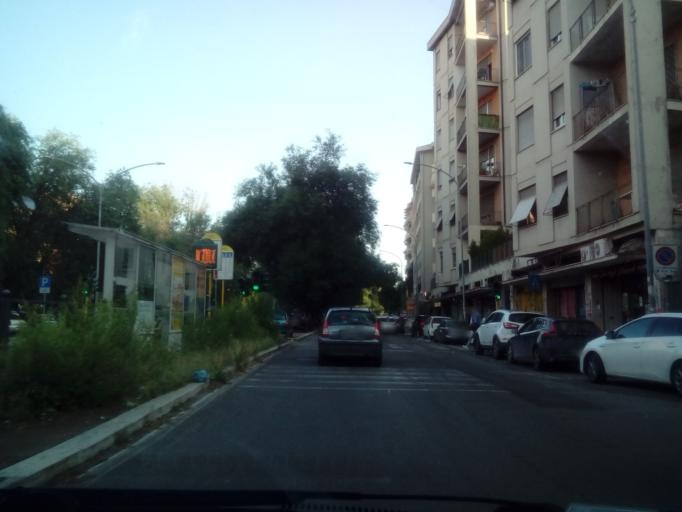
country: IT
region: Latium
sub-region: Citta metropolitana di Roma Capitale
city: Rome
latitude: 41.8576
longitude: 12.5707
